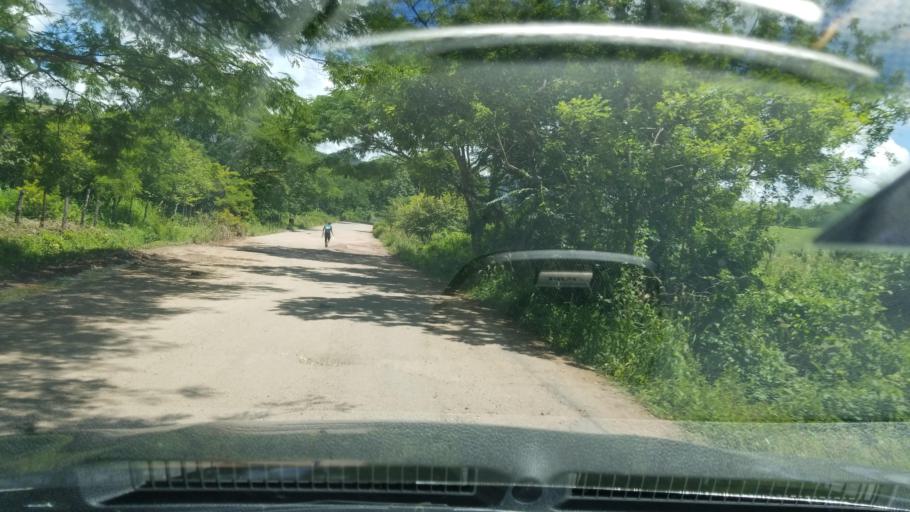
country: HN
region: Francisco Morazan
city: San Juan de Flores
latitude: 14.3119
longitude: -87.0367
